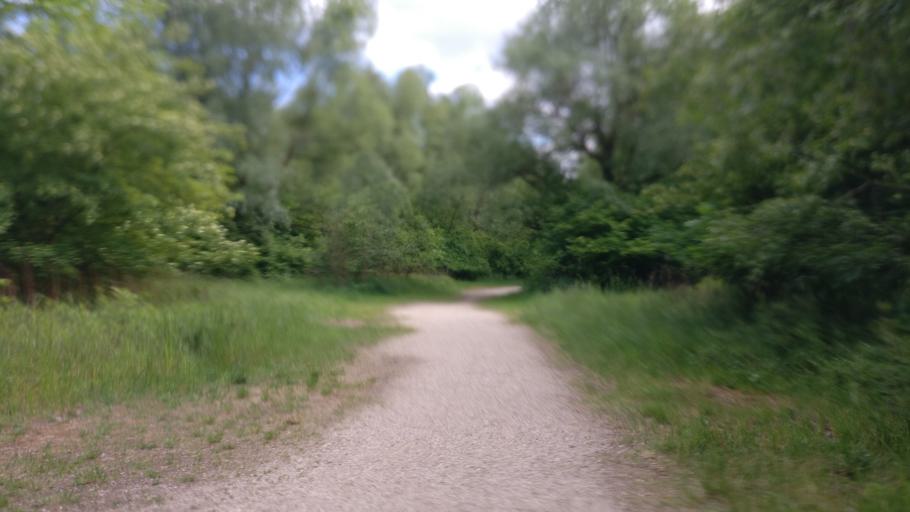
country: DE
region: North Rhine-Westphalia
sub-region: Regierungsbezirk Detmold
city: Lage
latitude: 52.0094
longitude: 8.7647
